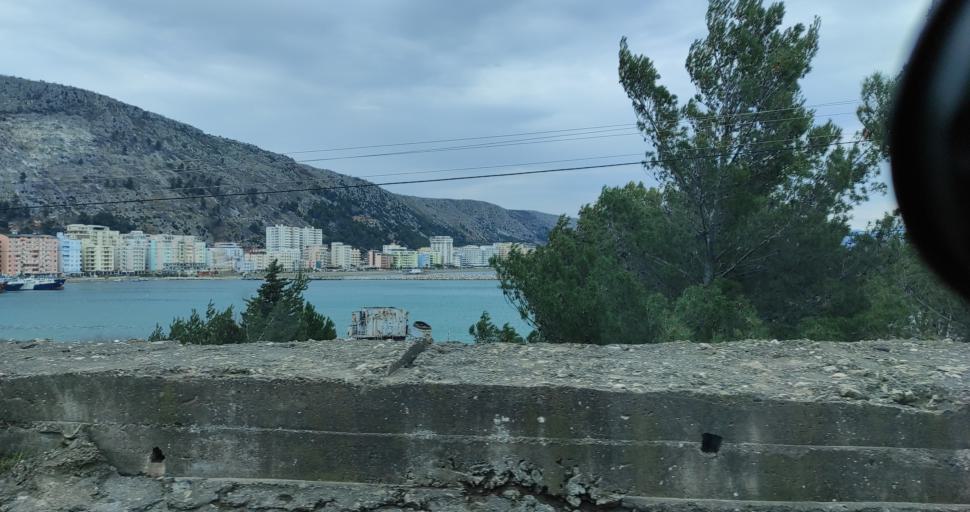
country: AL
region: Lezhe
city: Shengjin
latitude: 41.8119
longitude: 19.5848
